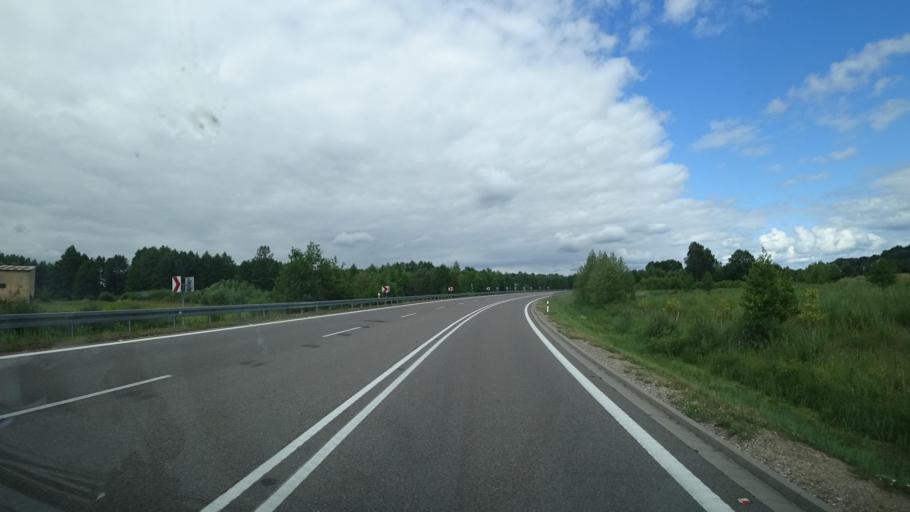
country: PL
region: Warmian-Masurian Voivodeship
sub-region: Powiat goldapski
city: Goldap
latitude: 54.3139
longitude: 22.2806
